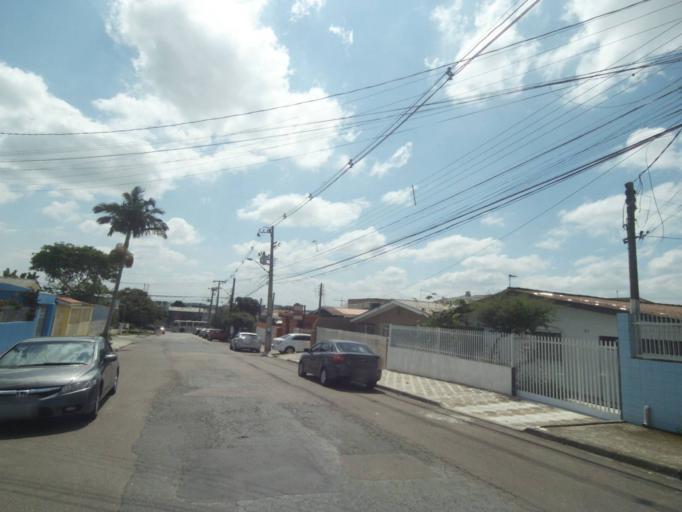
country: BR
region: Parana
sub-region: Curitiba
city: Curitiba
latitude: -25.5118
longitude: -49.3224
